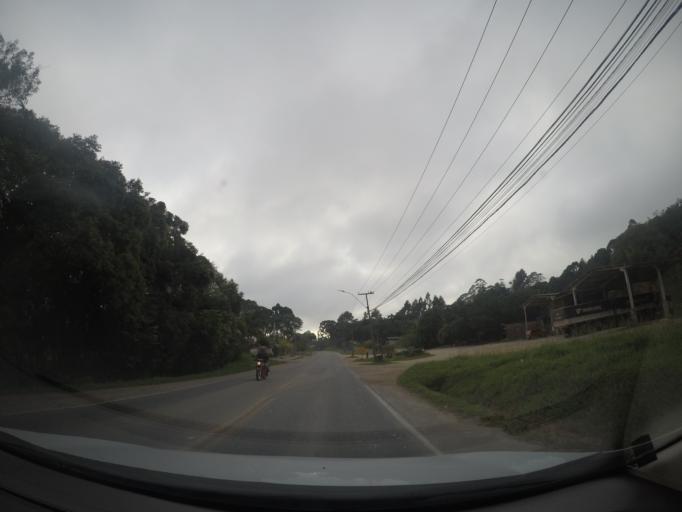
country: BR
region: Parana
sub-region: Colombo
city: Colombo
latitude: -25.2952
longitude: -49.2330
